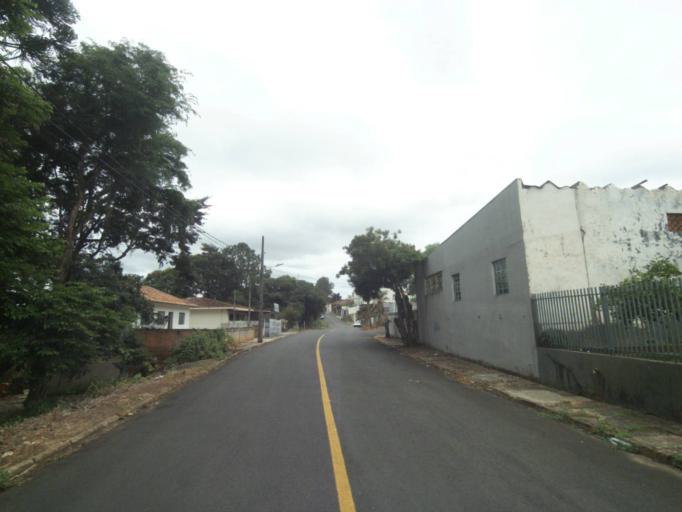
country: BR
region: Parana
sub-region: Telemaco Borba
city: Telemaco Borba
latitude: -24.3336
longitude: -50.6099
